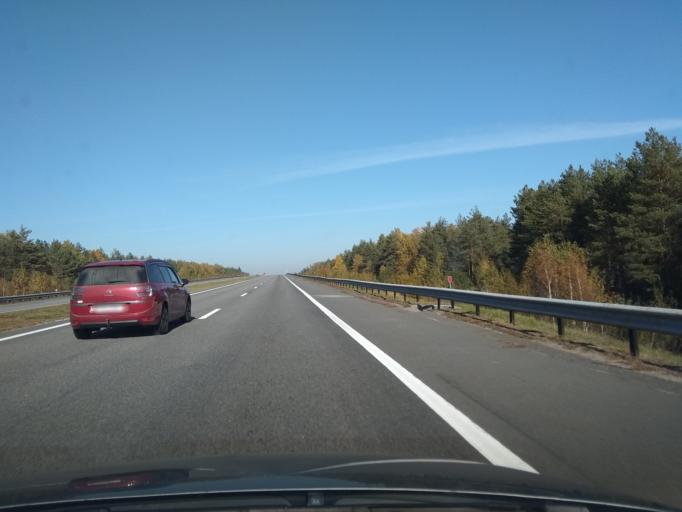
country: BY
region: Grodnenskaya
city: Zhyrovichy
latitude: 52.9072
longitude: 25.6792
